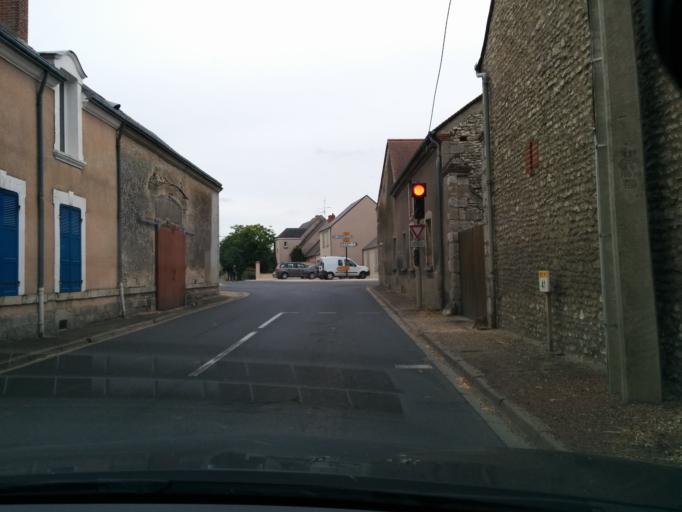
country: FR
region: Centre
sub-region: Departement du Loiret
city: Ascheres-le-Marche
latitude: 48.1083
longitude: 2.0065
